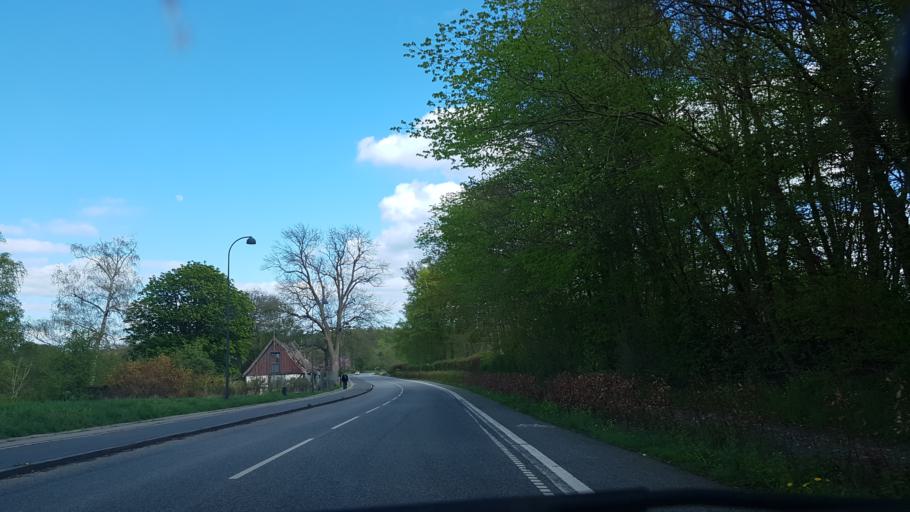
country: DK
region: Capital Region
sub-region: Rudersdal Kommune
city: Trorod
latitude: 55.8287
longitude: 12.5333
